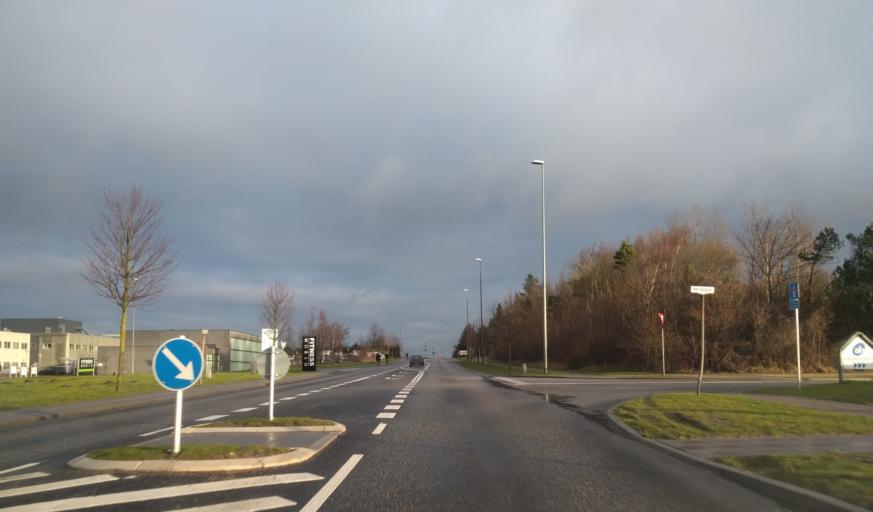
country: DK
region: North Denmark
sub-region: Alborg Kommune
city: Gistrup
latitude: 57.0281
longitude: 9.9764
